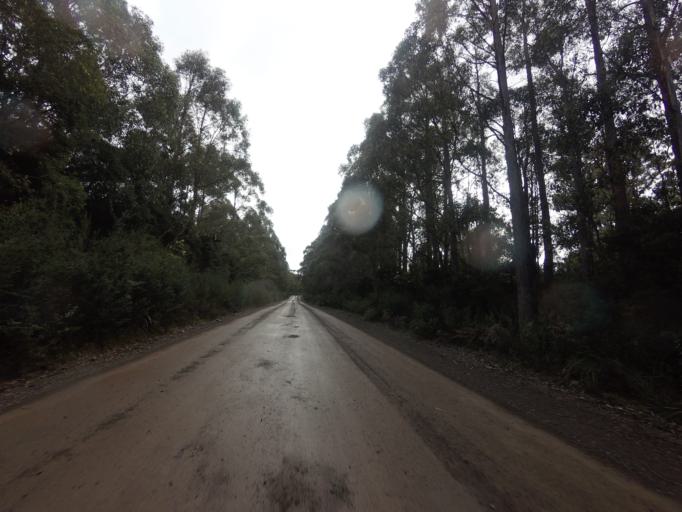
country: AU
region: Tasmania
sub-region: Huon Valley
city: Geeveston
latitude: -43.4626
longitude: 146.8998
